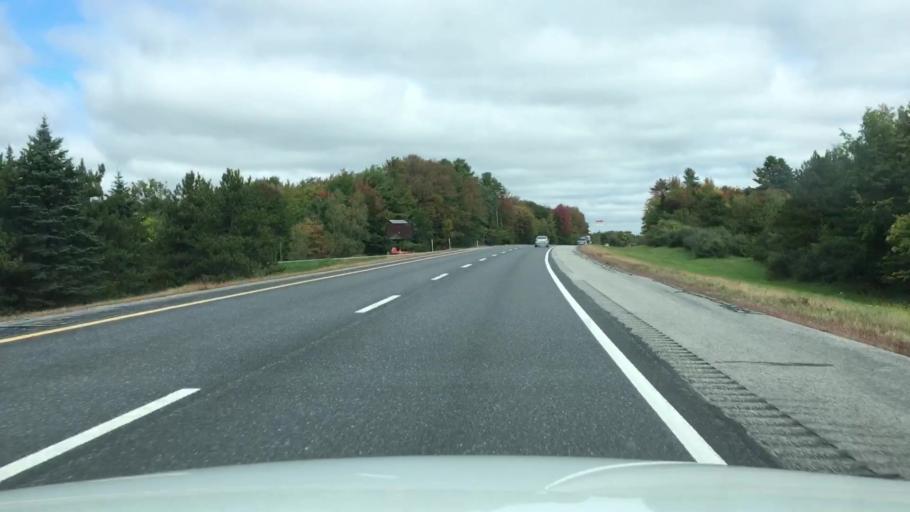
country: US
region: Maine
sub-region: Sagadahoc County
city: Topsham
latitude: 44.0252
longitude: -69.9161
